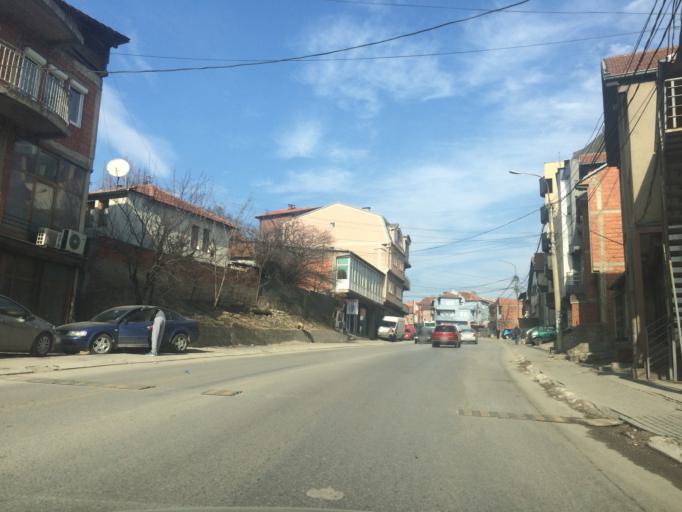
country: XK
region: Pristina
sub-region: Komuna e Prishtines
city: Pristina
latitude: 42.6734
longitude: 21.1638
